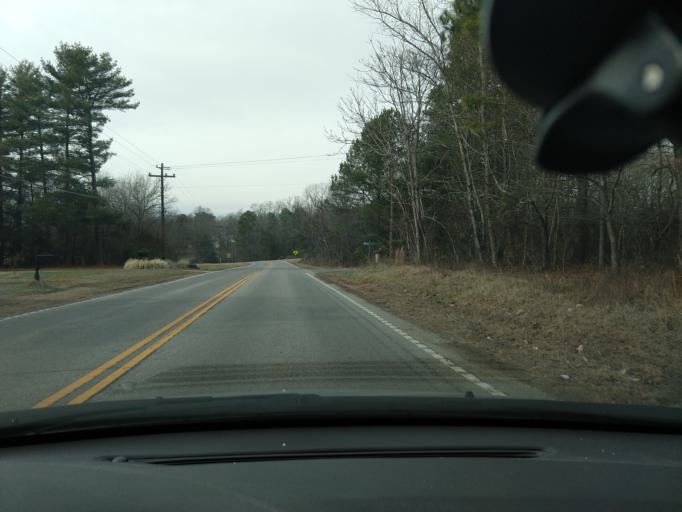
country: US
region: South Carolina
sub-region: Spartanburg County
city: Cowpens
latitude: 35.0099
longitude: -81.8683
